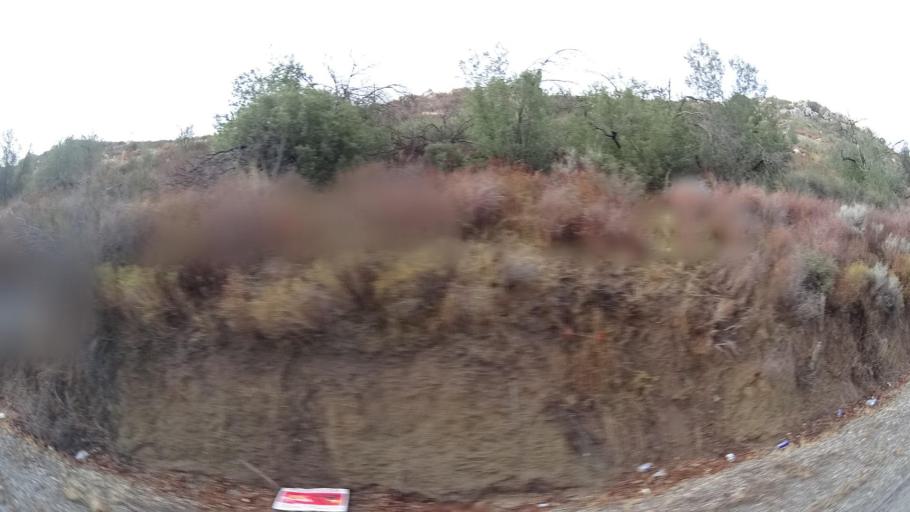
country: MX
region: Baja California
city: Tecate
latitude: 32.6085
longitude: -116.6270
